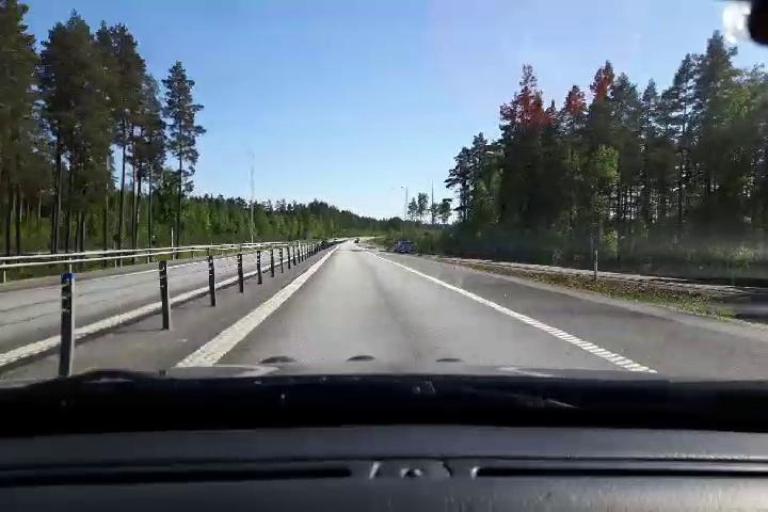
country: SE
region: Gaevleborg
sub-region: Gavle Kommun
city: Norrsundet
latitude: 61.0704
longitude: 16.9641
